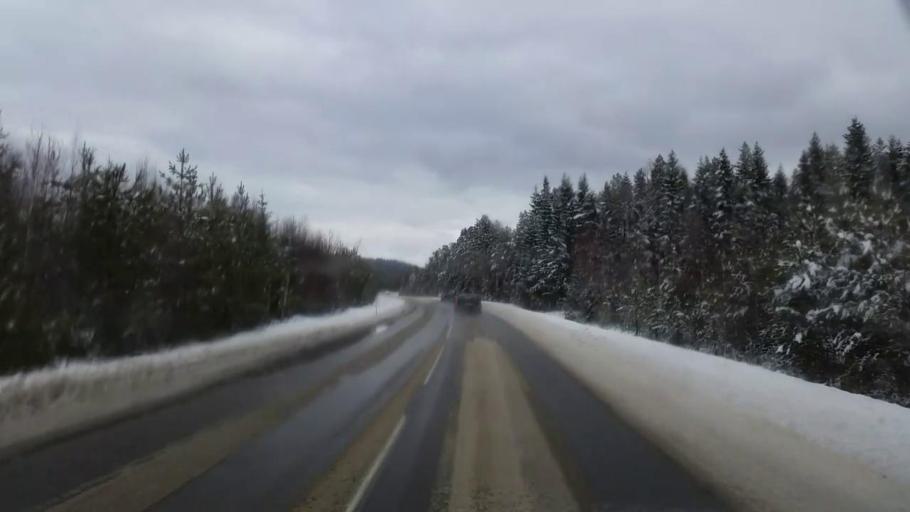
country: SE
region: Vaesternorrland
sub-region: Ange Kommun
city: Ange
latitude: 62.0453
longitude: 15.1667
